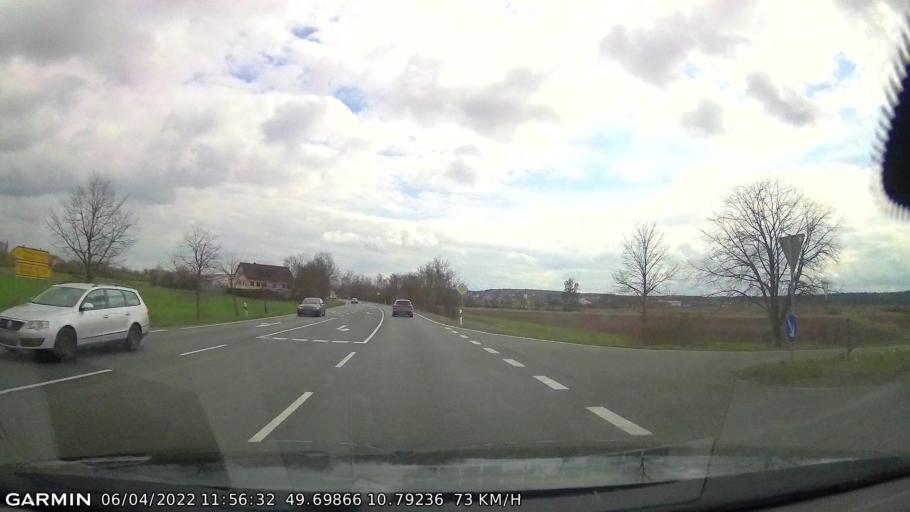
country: DE
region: Bavaria
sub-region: Regierungsbezirk Mittelfranken
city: Hochstadt an der Aisch
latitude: 49.6987
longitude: 10.7925
